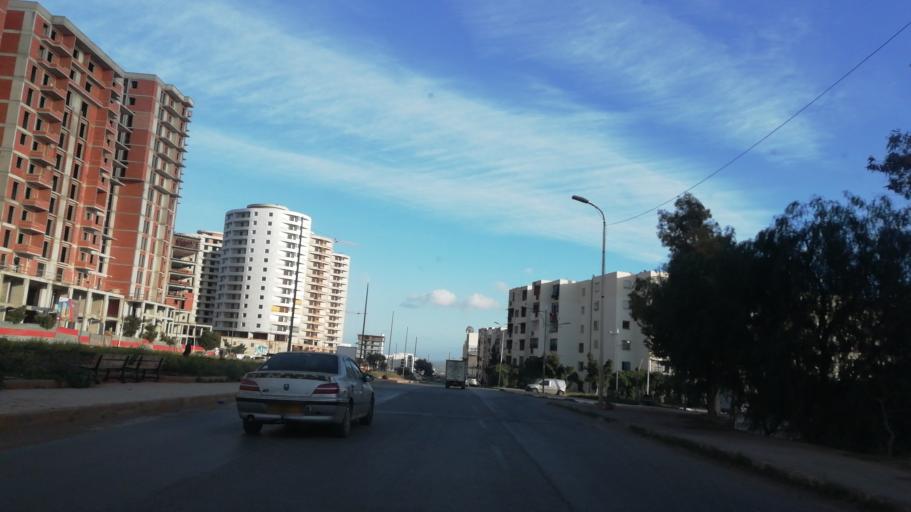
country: DZ
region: Oran
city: Bir el Djir
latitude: 35.7090
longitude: -0.5648
